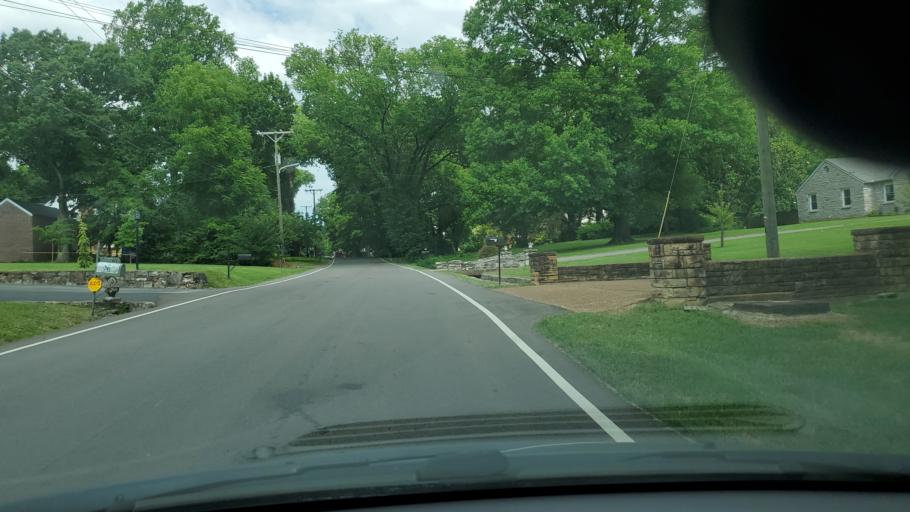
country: US
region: Tennessee
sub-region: Davidson County
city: Lakewood
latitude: 36.2259
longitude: -86.7177
